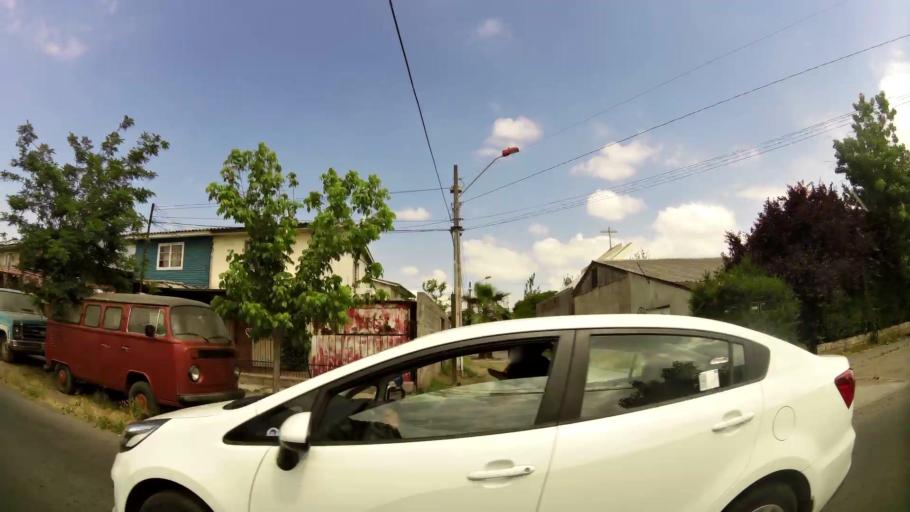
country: CL
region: Santiago Metropolitan
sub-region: Provincia de Santiago
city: Santiago
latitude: -33.5026
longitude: -70.6840
